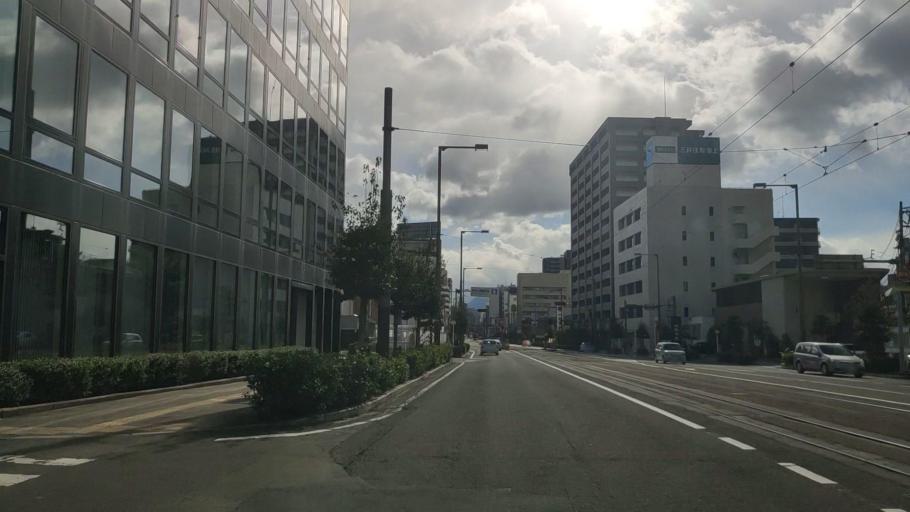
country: JP
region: Ehime
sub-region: Shikoku-chuo Shi
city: Matsuyama
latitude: 33.8453
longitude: 132.7755
